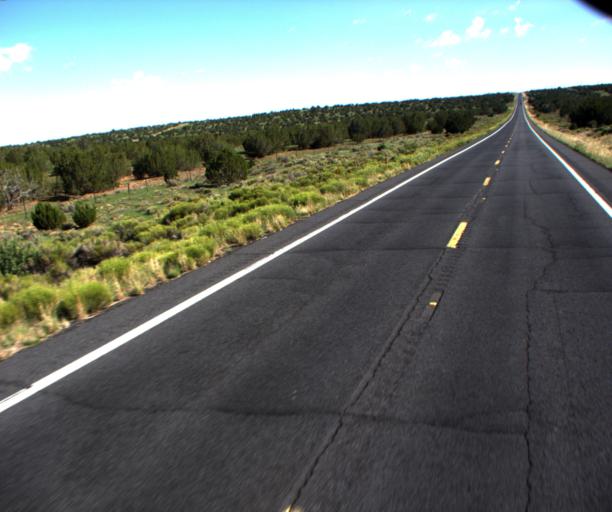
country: US
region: Arizona
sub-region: Coconino County
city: Williams
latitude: 35.5125
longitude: -112.1721
